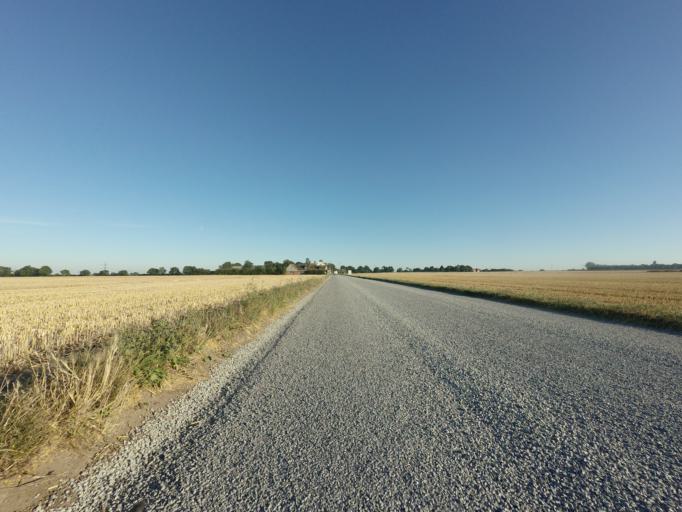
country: GB
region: England
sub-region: Kent
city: Herne Bay
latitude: 51.3383
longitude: 1.1900
